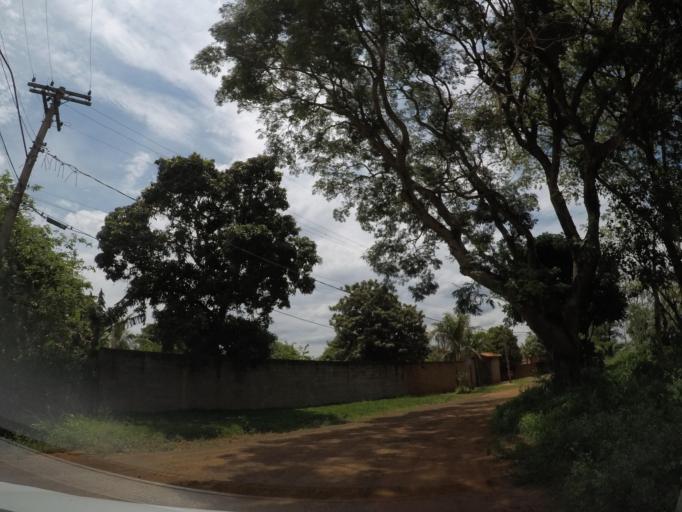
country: BR
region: Sao Paulo
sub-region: Sumare
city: Sumare
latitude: -22.8485
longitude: -47.2970
